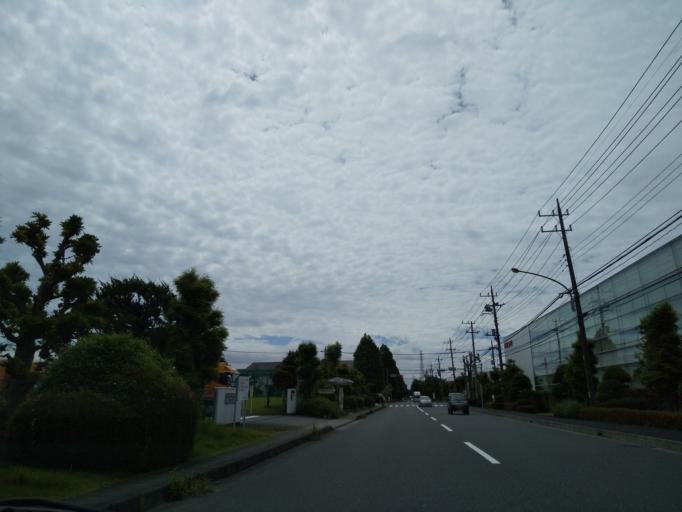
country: JP
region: Kanagawa
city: Zama
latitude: 35.5136
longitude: 139.3442
